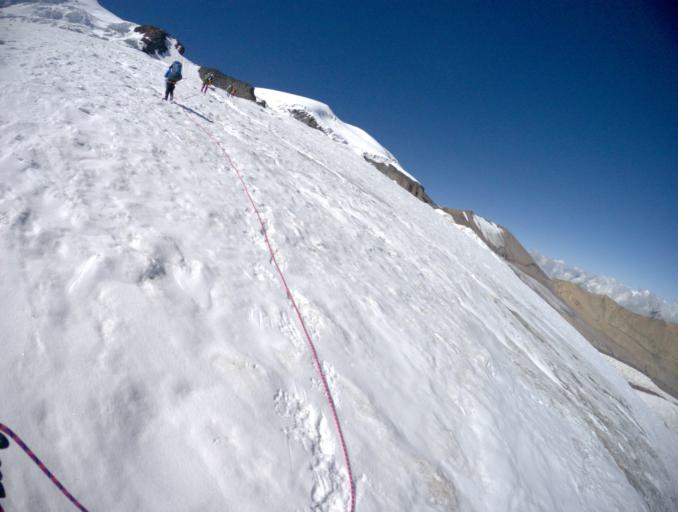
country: RU
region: Kabardino-Balkariya
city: Terskol
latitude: 43.3838
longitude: 42.4367
